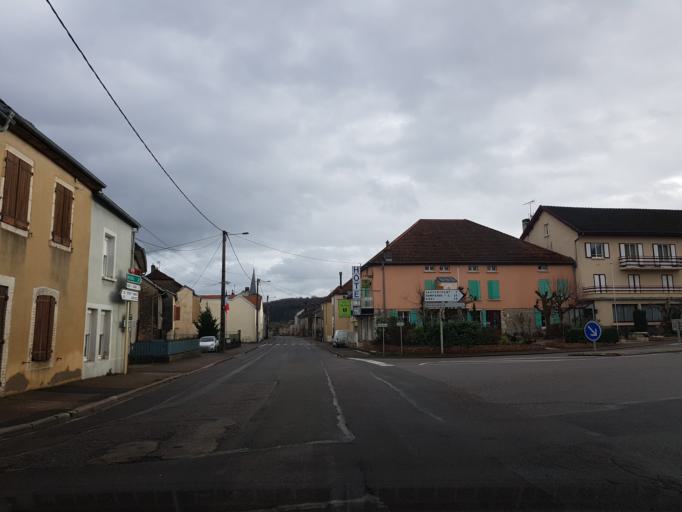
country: FR
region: Franche-Comte
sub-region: Departement de la Haute-Saone
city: Scey-sur-Saone-et-Saint-Albin
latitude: 47.7123
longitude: 5.8877
